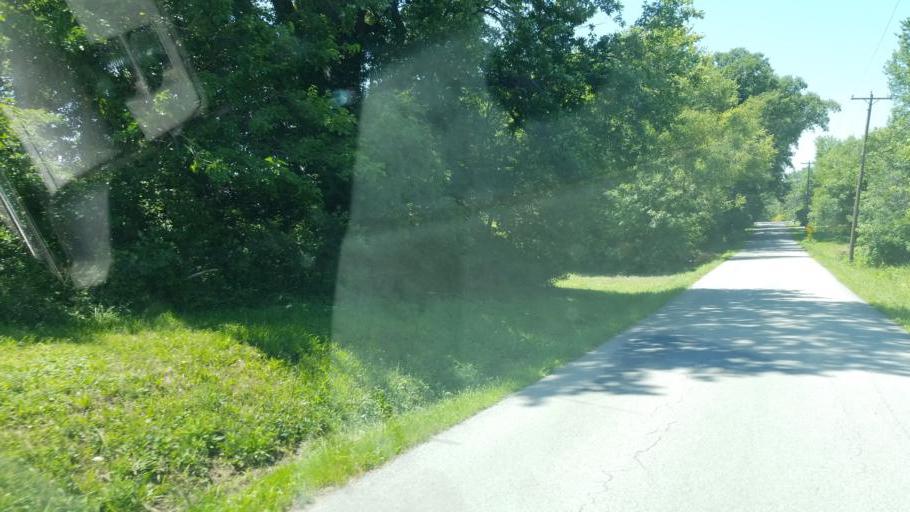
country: US
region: Ohio
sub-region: Sandusky County
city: Fremont
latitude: 41.4035
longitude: -83.0779
